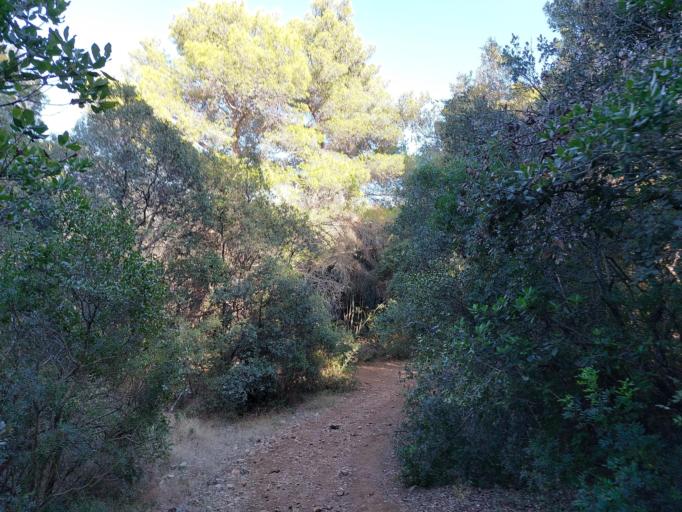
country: HR
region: Dubrovacko-Neretvanska
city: Smokvica
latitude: 42.7582
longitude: 16.8086
